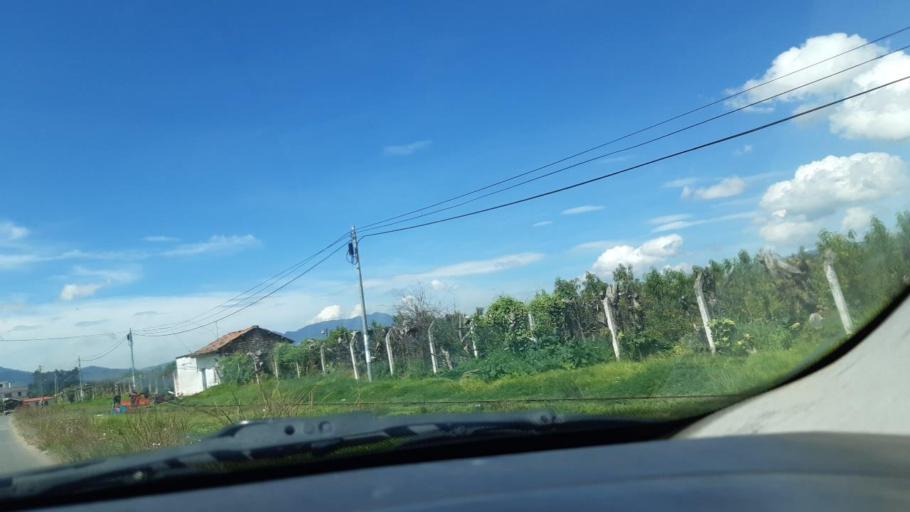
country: GT
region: Quetzaltenango
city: Salcaja
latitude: 14.8799
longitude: -91.4469
